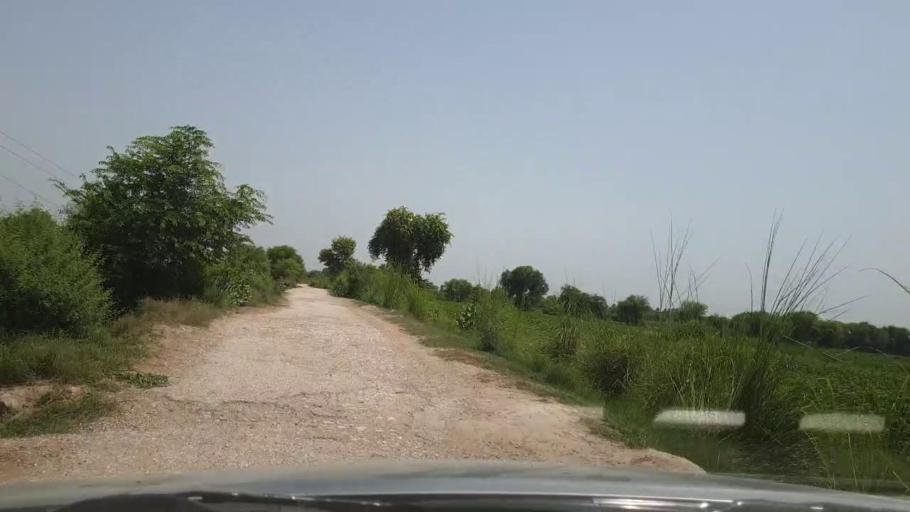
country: PK
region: Sindh
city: Pano Aqil
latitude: 27.8201
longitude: 69.2289
